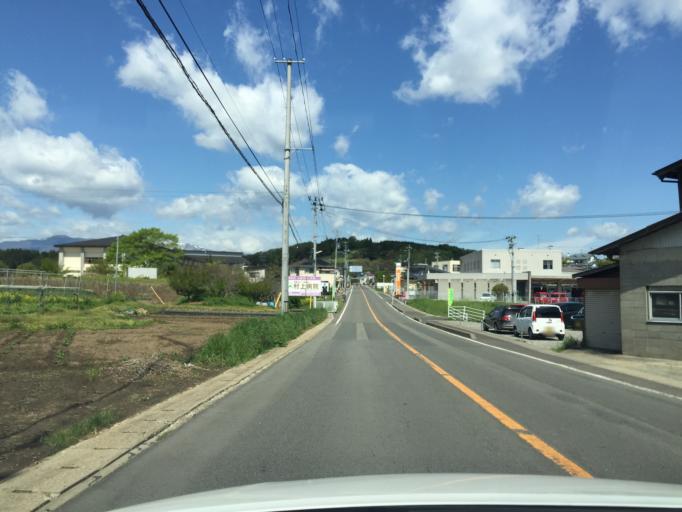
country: JP
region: Fukushima
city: Nihommatsu
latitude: 37.6575
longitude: 140.4699
